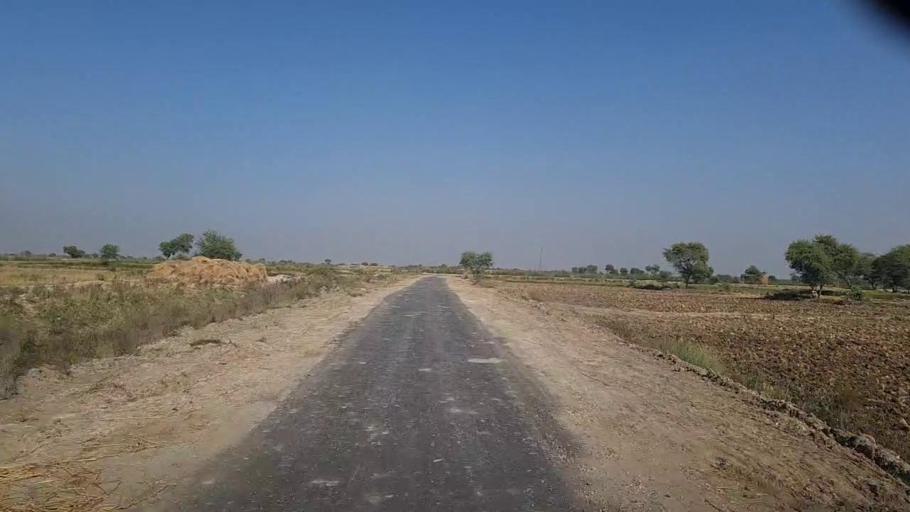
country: PK
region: Sindh
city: Tangwani
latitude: 28.2669
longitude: 68.9371
